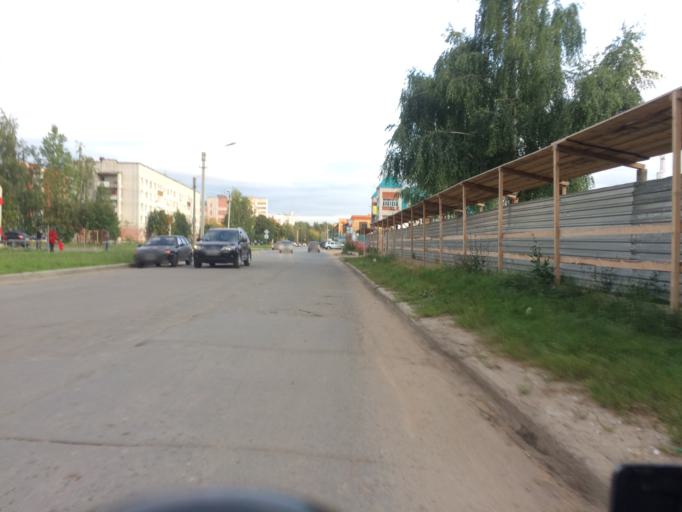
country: RU
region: Mariy-El
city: Medvedevo
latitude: 56.6453
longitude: 47.8348
